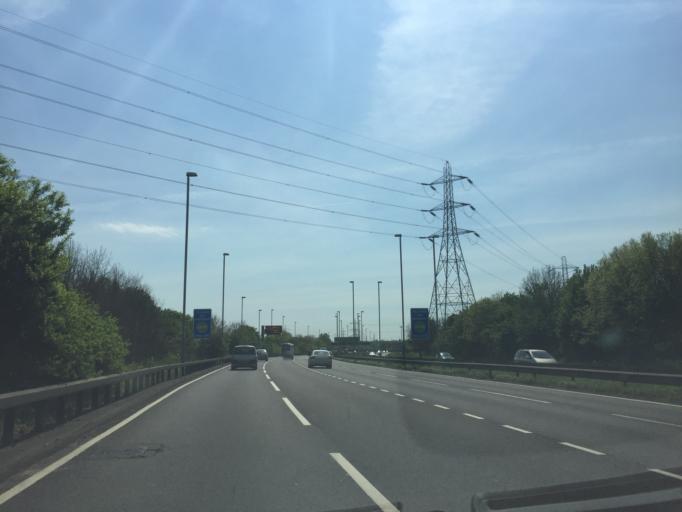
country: GB
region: England
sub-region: Greater London
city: Woodford Green
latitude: 51.5877
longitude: 0.0400
